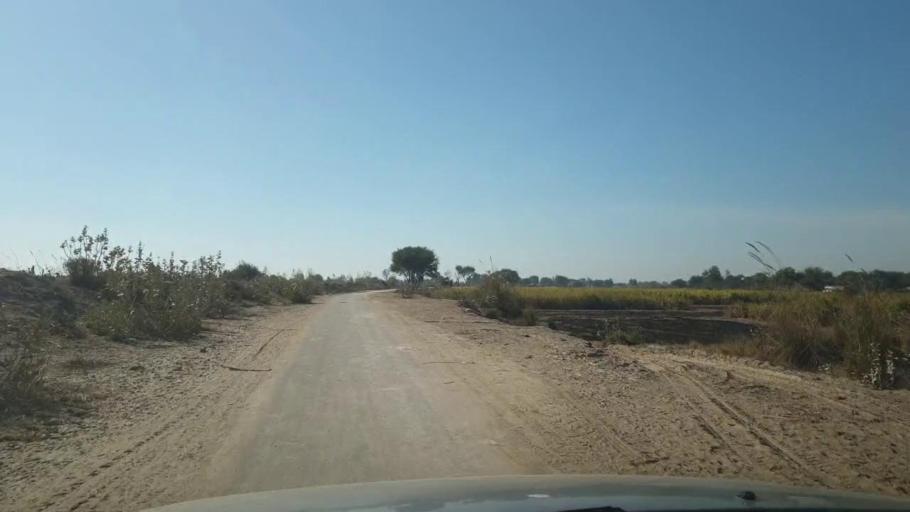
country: PK
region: Sindh
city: Ghotki
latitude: 28.0186
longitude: 69.2676
